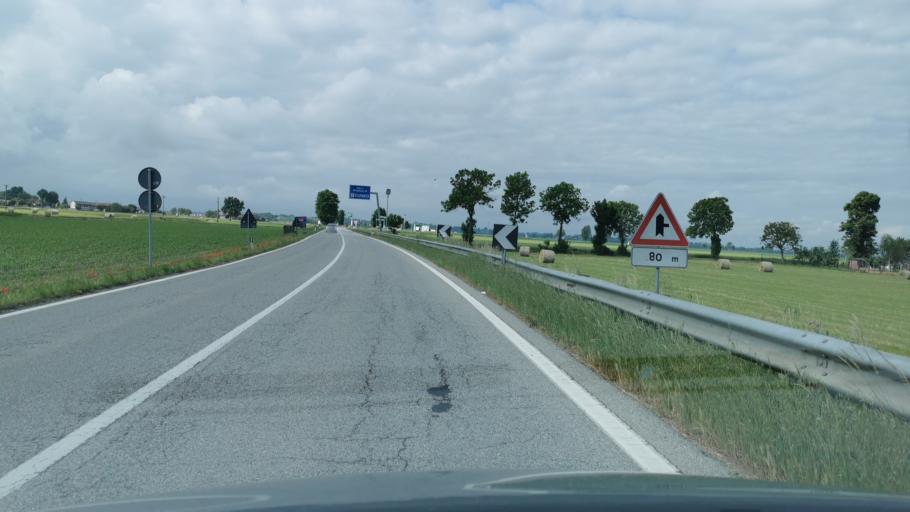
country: IT
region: Piedmont
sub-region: Provincia di Torino
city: Carmagnola
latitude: 44.8146
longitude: 7.7010
